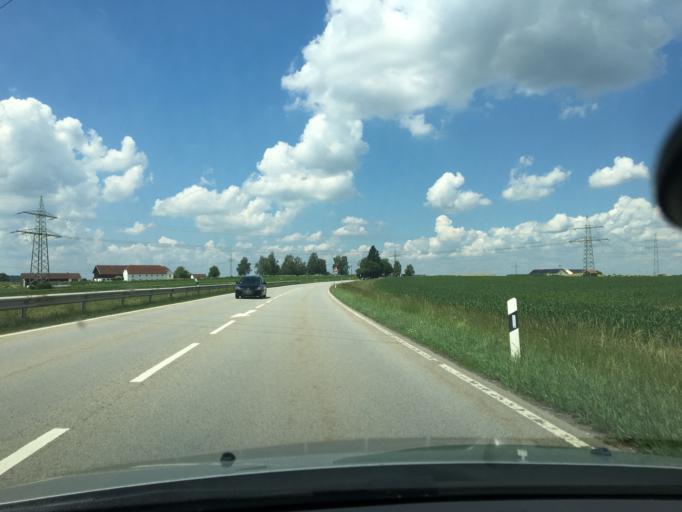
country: DE
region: Bavaria
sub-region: Upper Bavaria
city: Burgkirchen an der Alz
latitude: 48.1513
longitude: 12.7556
